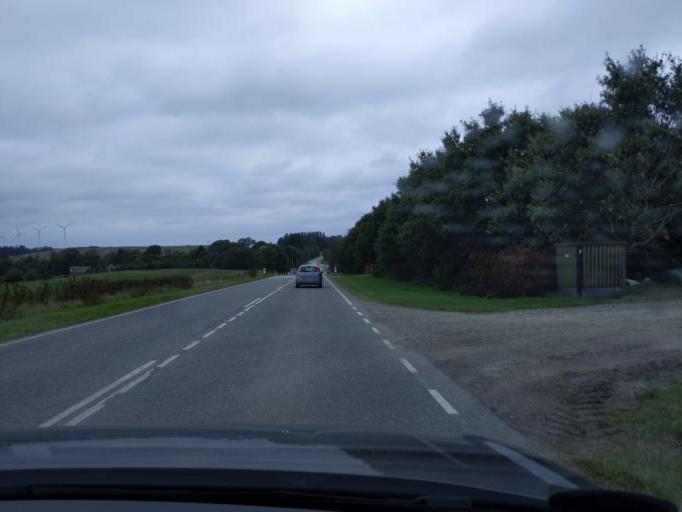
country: DK
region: North Denmark
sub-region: Mariagerfjord Kommune
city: Hobro
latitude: 56.5675
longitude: 9.8268
